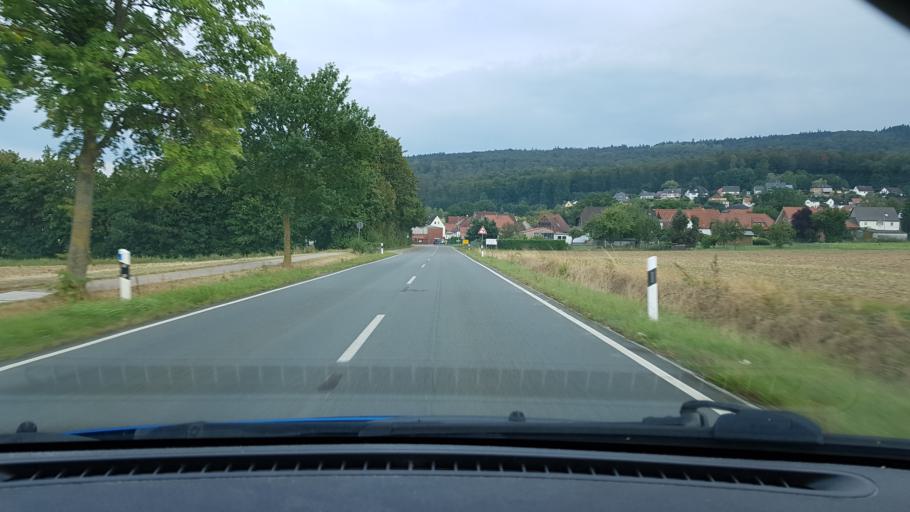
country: DE
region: Lower Saxony
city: Bad Munder am Deister
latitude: 52.1980
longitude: 9.4044
